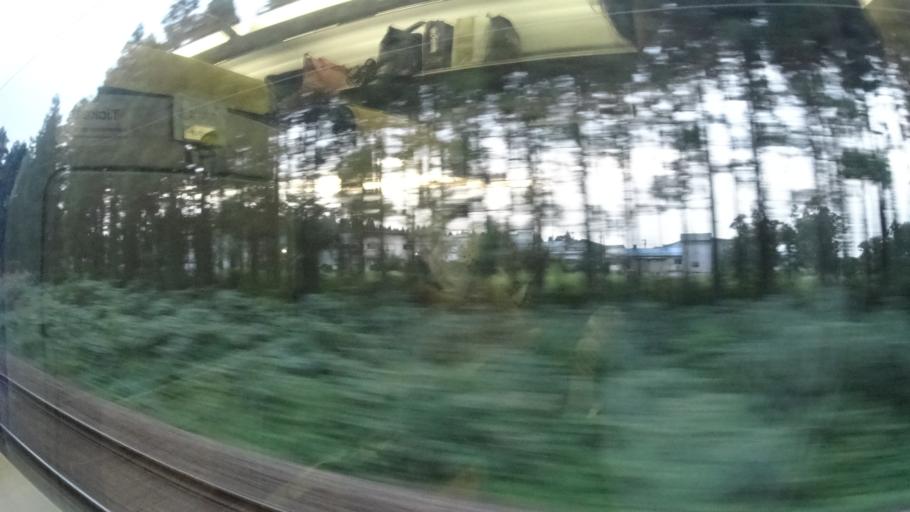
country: JP
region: Niigata
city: Murakami
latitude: 38.1081
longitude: 139.4371
